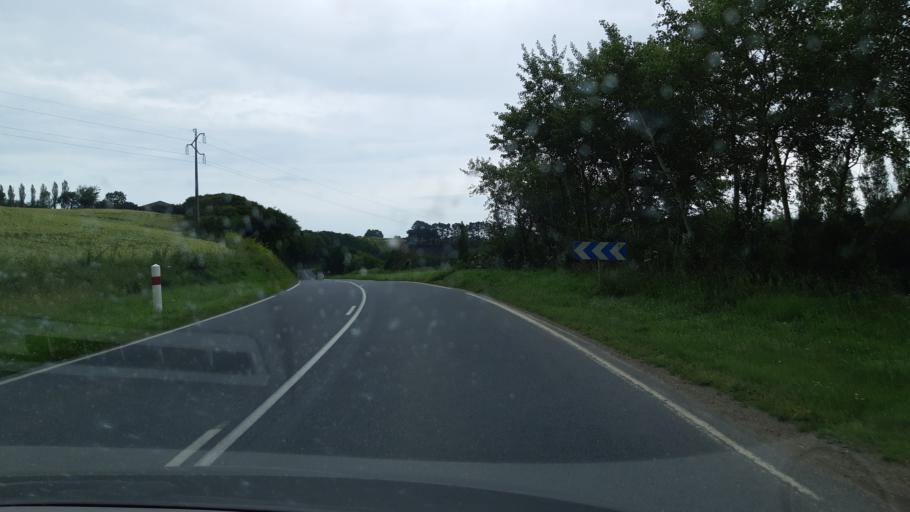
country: FR
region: Brittany
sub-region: Departement du Finistere
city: Plougoulm
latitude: 48.6513
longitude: -4.0378
